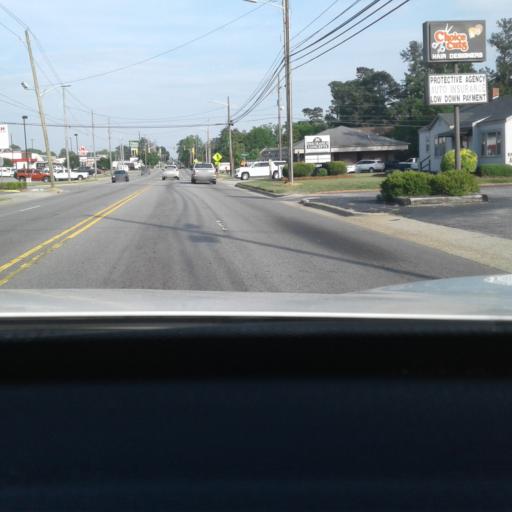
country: US
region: North Carolina
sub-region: Harnett County
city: Dunn
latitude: 35.3140
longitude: -78.6224
